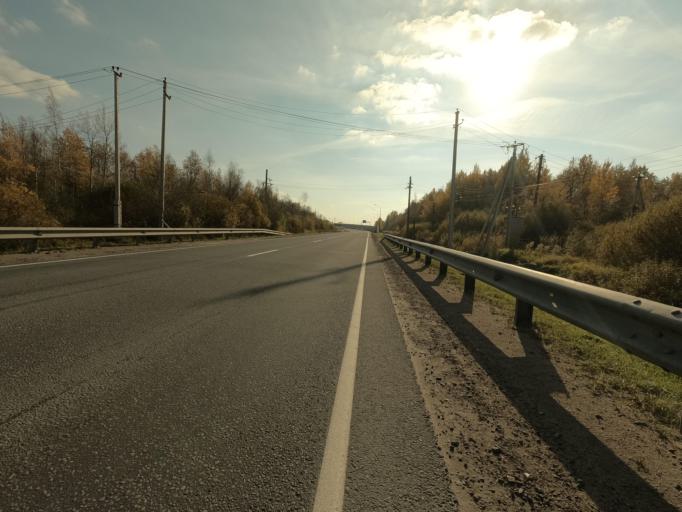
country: RU
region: Leningrad
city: Mga
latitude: 59.7638
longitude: 31.0949
